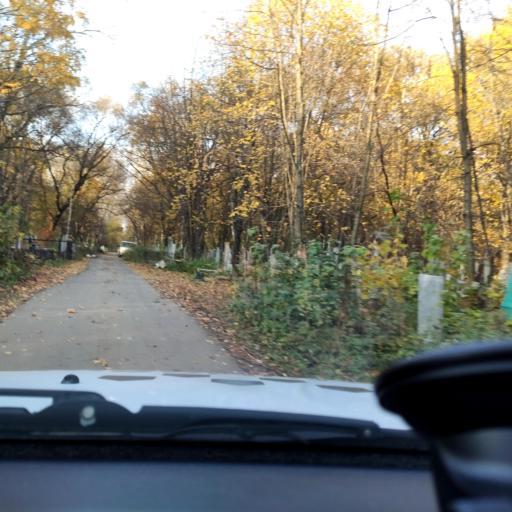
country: RU
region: Perm
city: Perm
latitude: 57.9892
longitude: 56.2813
